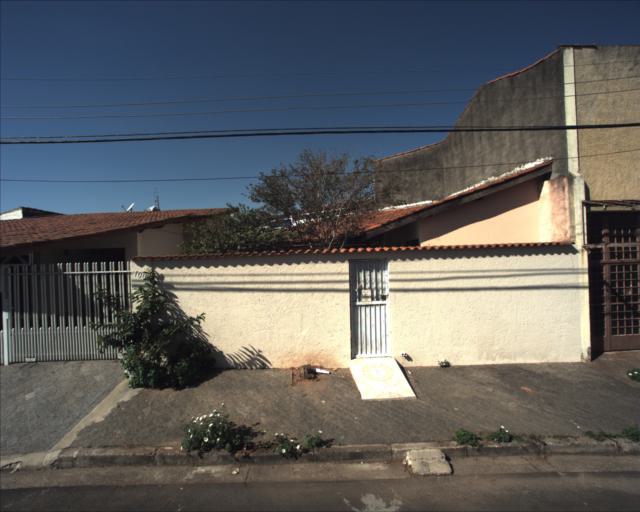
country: BR
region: Sao Paulo
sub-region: Sorocaba
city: Sorocaba
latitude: -23.4943
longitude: -47.4247
